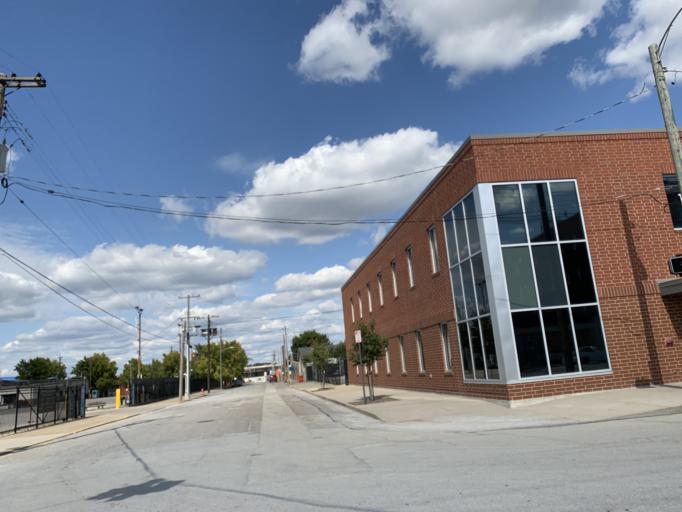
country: US
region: Kentucky
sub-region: Jefferson County
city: Louisville
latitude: 38.2565
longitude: -85.7683
